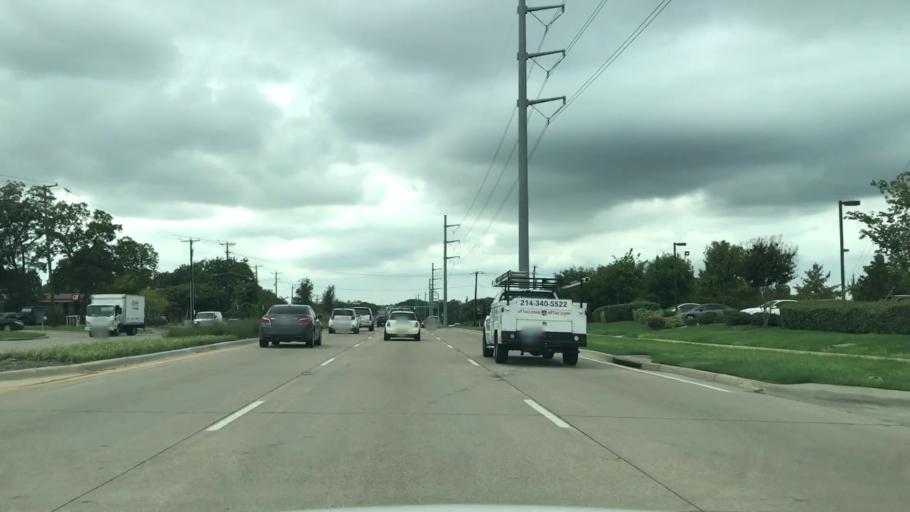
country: US
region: Texas
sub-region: Dallas County
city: Rowlett
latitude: 32.9084
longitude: -96.5823
